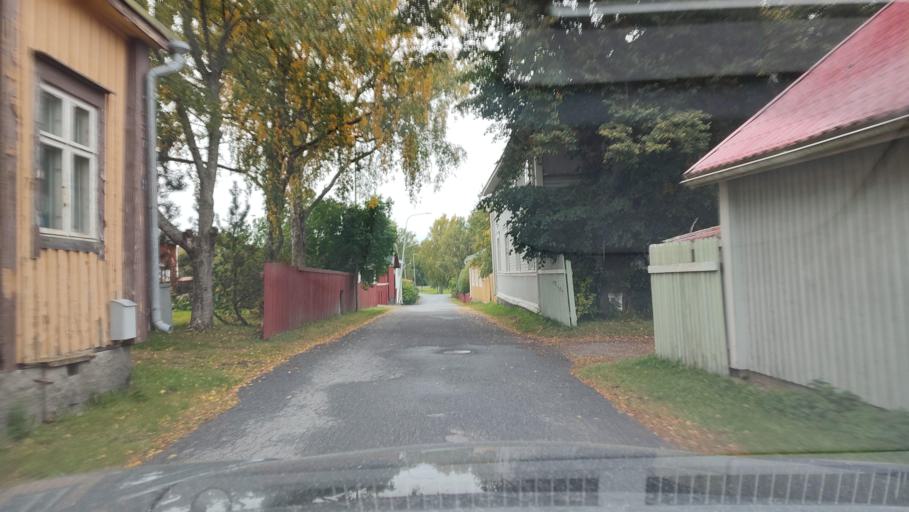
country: FI
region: Ostrobothnia
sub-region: Sydosterbotten
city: Kristinestad
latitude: 62.2790
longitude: 21.3775
